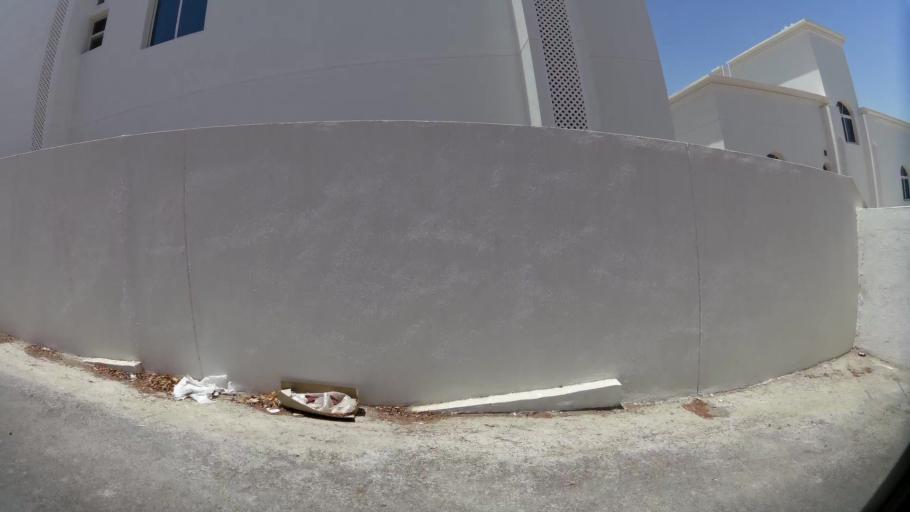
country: OM
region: Muhafazat Masqat
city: Bawshar
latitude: 23.6084
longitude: 58.4663
